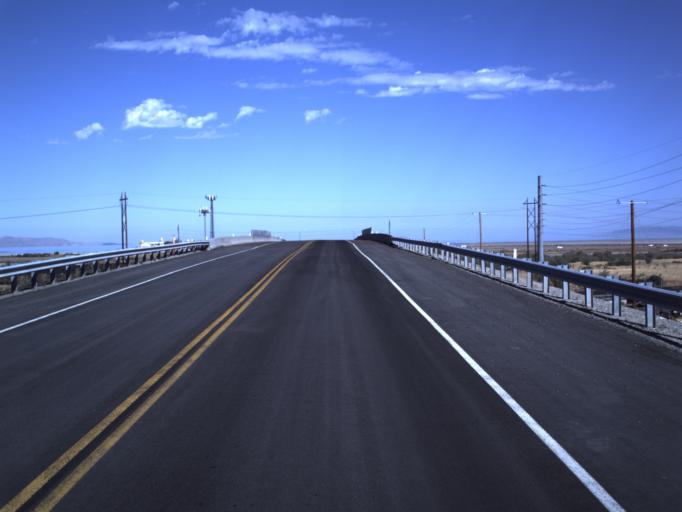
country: US
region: Utah
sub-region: Salt Lake County
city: Magna
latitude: 40.7402
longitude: -112.1769
